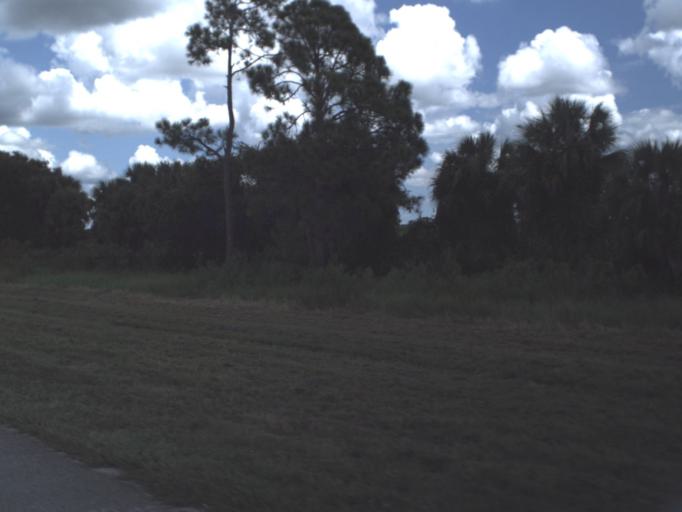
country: US
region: Florida
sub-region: Hendry County
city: Port LaBelle
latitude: 26.5906
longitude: -81.4367
